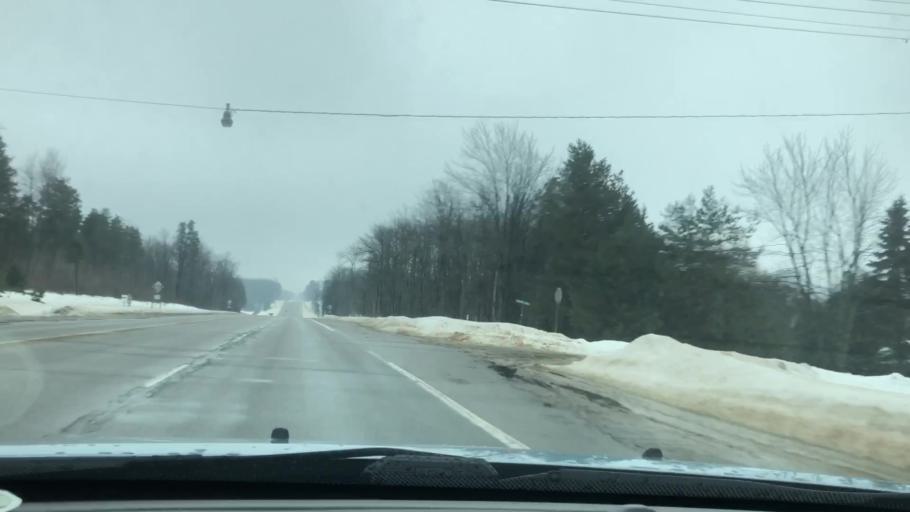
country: US
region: Michigan
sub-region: Otsego County
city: Gaylord
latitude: 45.0577
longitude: -84.7760
